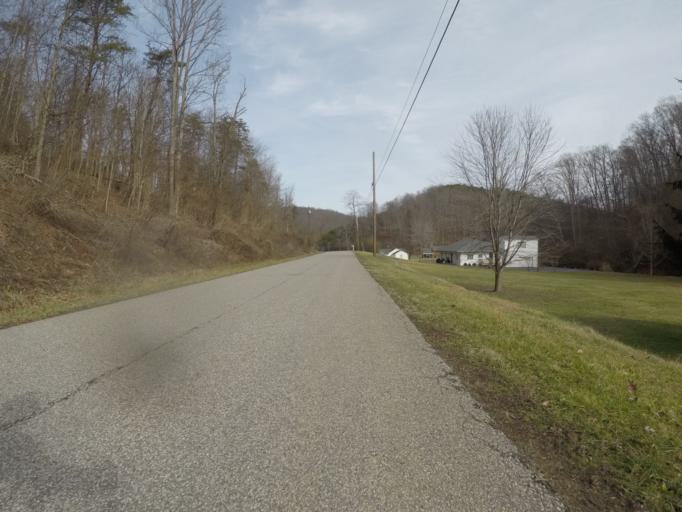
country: US
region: West Virginia
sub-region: Cabell County
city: Pea Ridge
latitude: 38.3569
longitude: -82.3726
